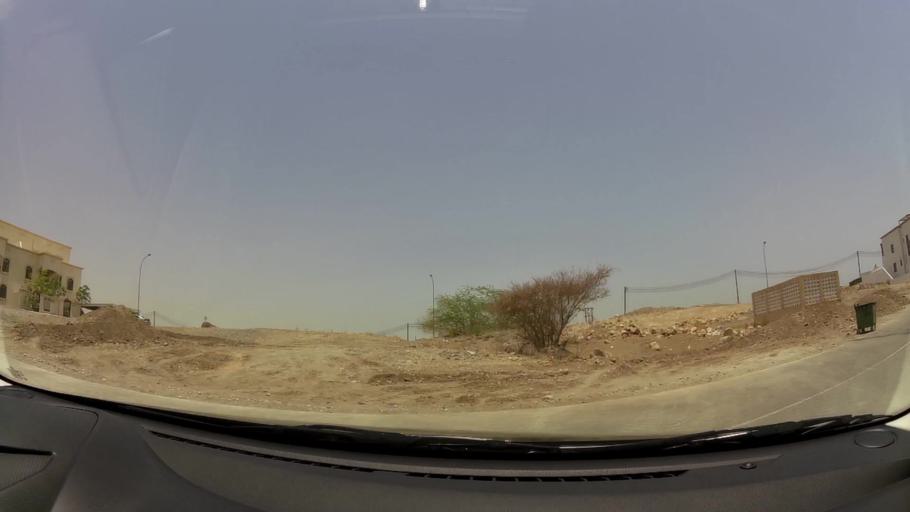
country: OM
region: Muhafazat Masqat
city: Bawshar
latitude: 23.5562
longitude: 58.4128
